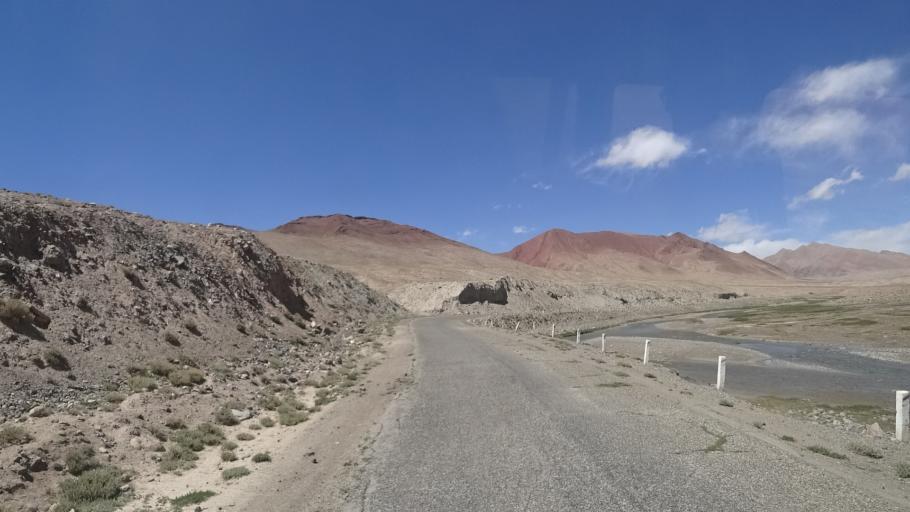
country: TJ
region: Gorno-Badakhshan
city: Murghob
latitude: 38.4929
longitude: 73.8417
